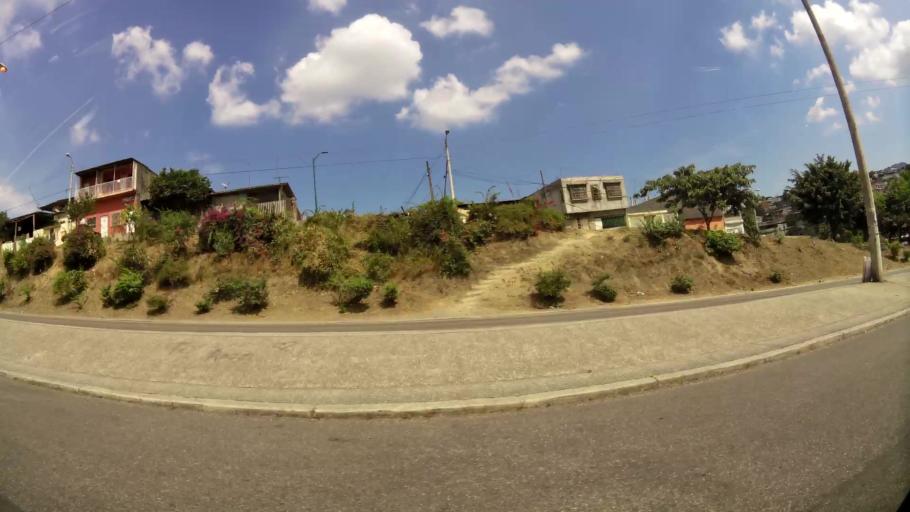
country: EC
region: Guayas
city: Santa Lucia
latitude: -2.1294
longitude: -79.9479
